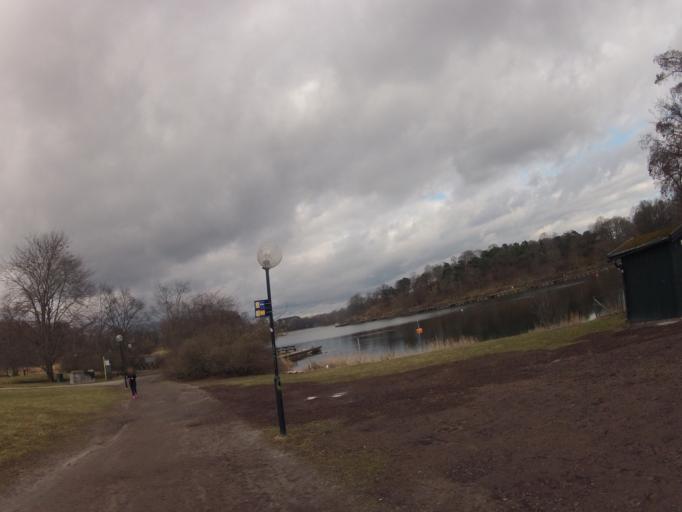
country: SE
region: Stockholm
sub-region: Norrtalje Kommun
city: Bergshamra
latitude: 59.3527
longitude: 18.0432
